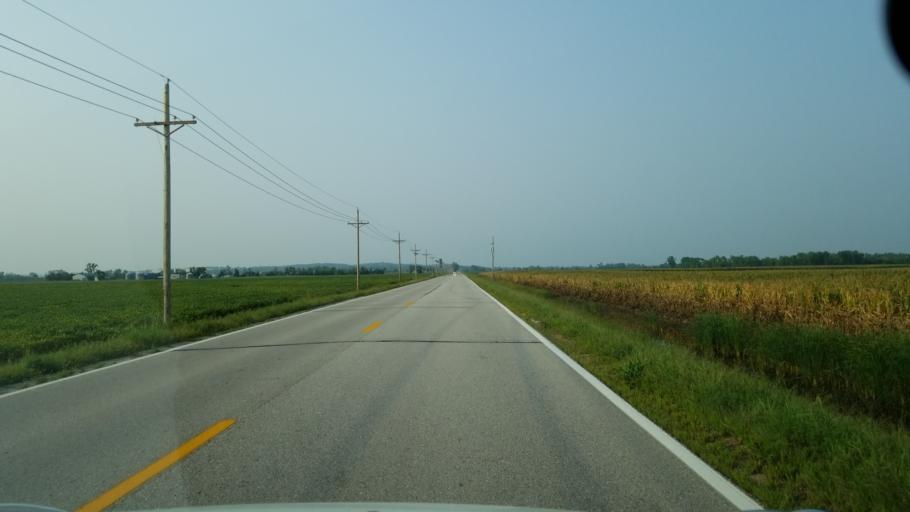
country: US
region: Nebraska
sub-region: Sarpy County
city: Offutt Air Force Base
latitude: 41.0878
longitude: -95.8898
